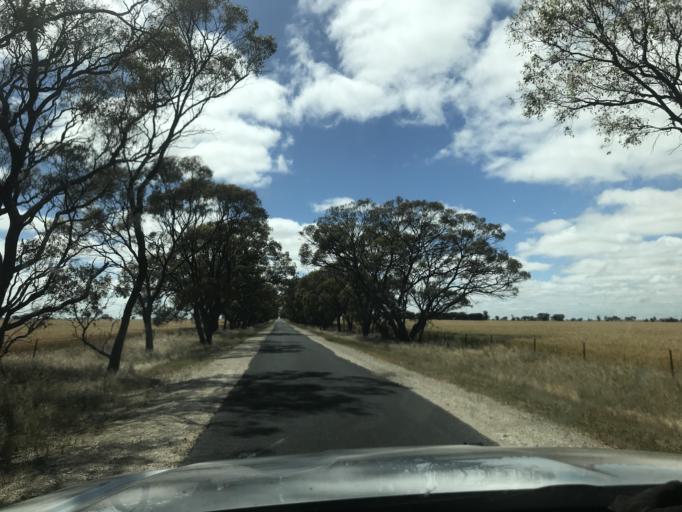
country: AU
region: South Australia
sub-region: Tatiara
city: Bordertown
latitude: -36.2780
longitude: 141.1112
